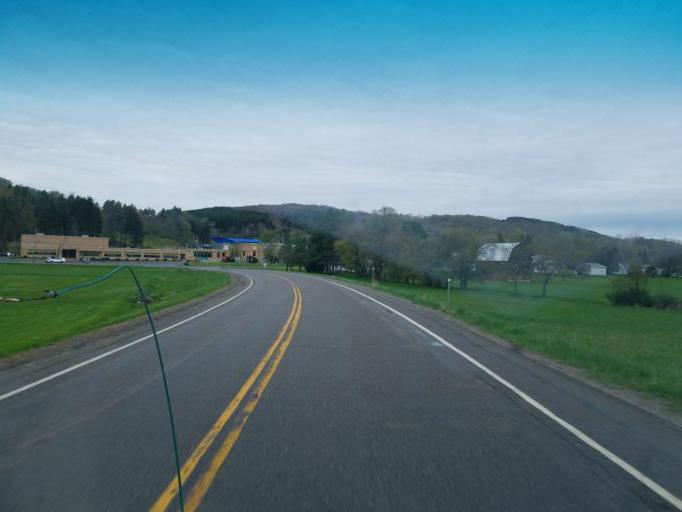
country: US
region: New York
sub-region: Allegany County
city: Andover
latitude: 42.0364
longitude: -77.7811
